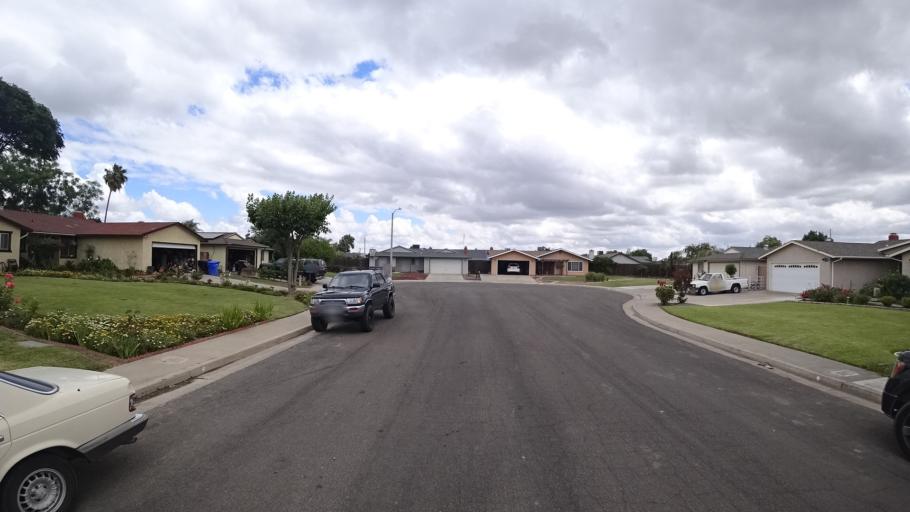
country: US
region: California
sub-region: Kings County
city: Hanford
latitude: 36.3345
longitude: -119.6260
